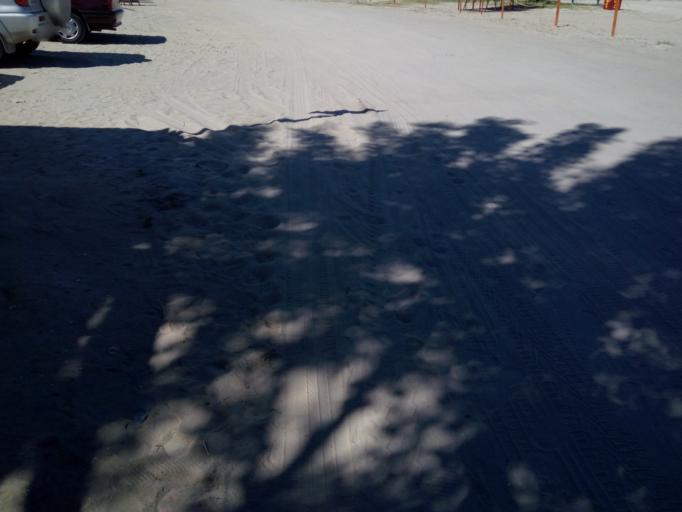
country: RU
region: Rostov
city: Bataysk
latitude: 47.1566
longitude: 39.7719
